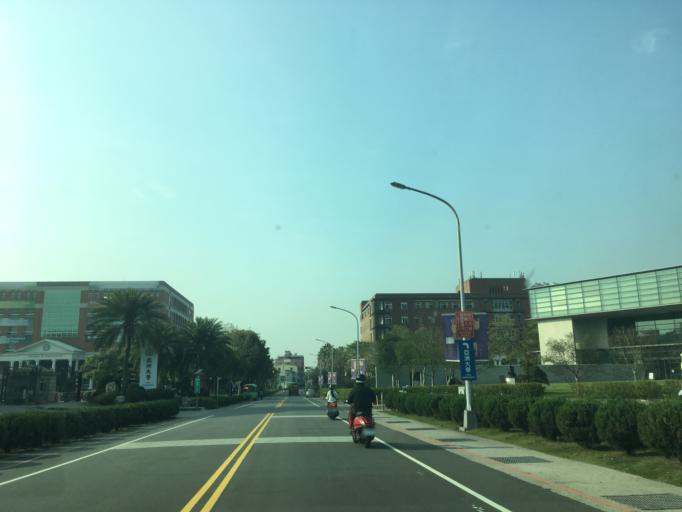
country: TW
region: Taiwan
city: Zhongxing New Village
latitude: 24.0460
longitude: 120.6878
